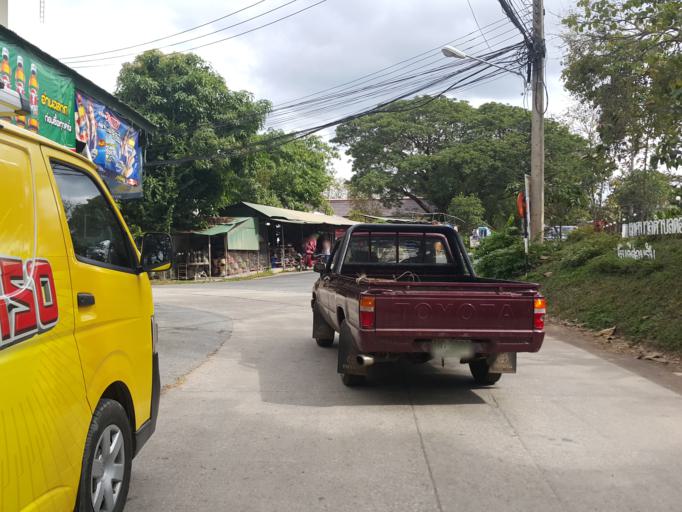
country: TH
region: Chiang Mai
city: San Sai
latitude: 18.8752
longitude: 99.1390
